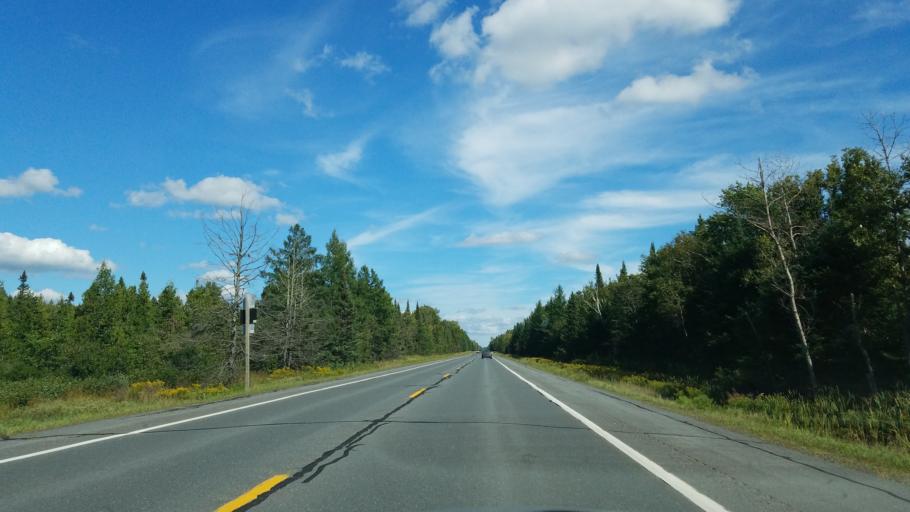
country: US
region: Michigan
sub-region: Baraga County
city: L'Anse
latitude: 46.5788
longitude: -88.4379
